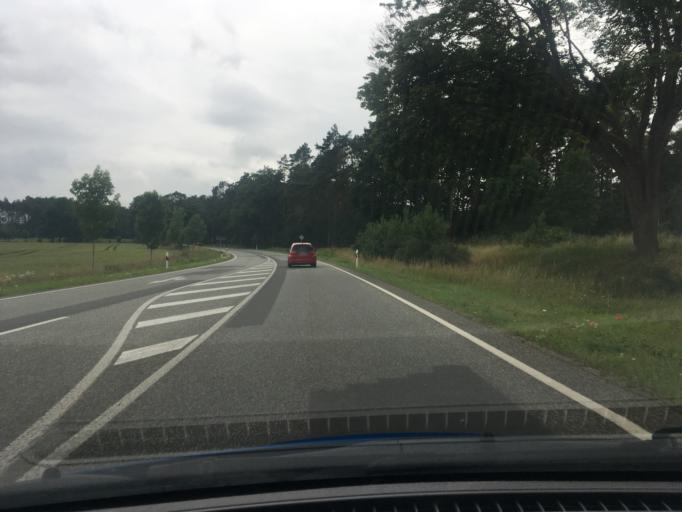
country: DE
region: Mecklenburg-Vorpommern
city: Stralendorf
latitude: 53.5609
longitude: 11.3452
